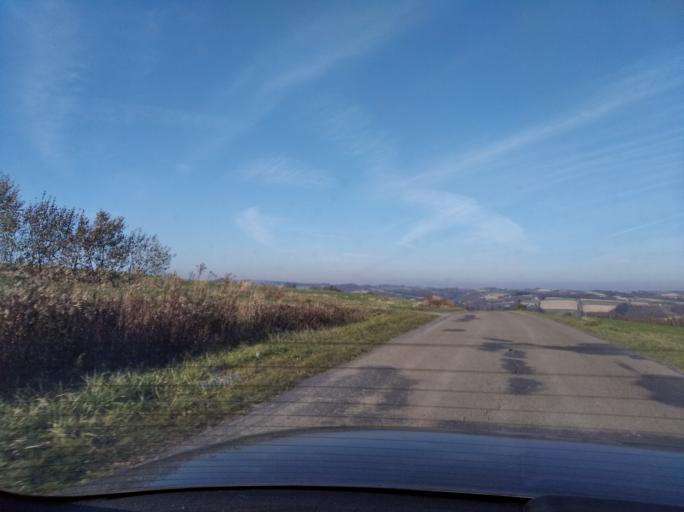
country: PL
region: Subcarpathian Voivodeship
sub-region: Powiat ropczycko-sedziszowski
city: Wielopole Skrzynskie
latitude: 49.9163
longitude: 21.5661
